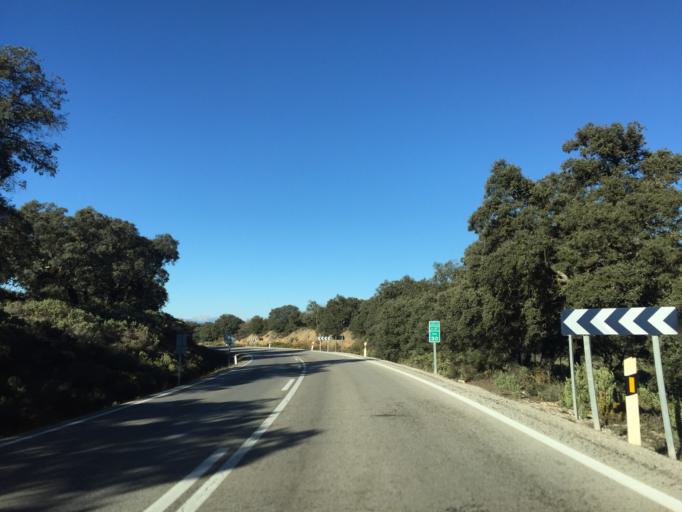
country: ES
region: Andalusia
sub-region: Provincia de Malaga
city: Cuevas del Becerro
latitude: 36.8314
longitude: -5.0841
